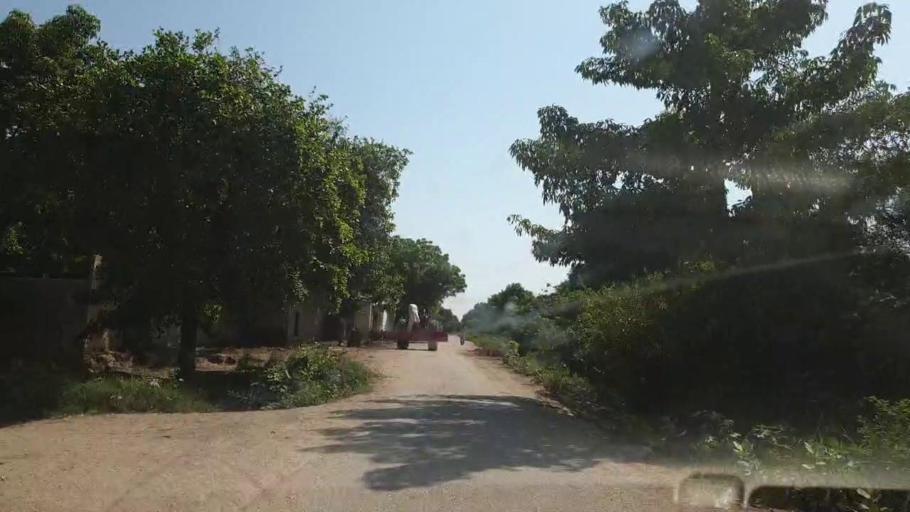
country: PK
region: Sindh
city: Tando Jam
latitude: 25.4113
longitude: 68.5821
